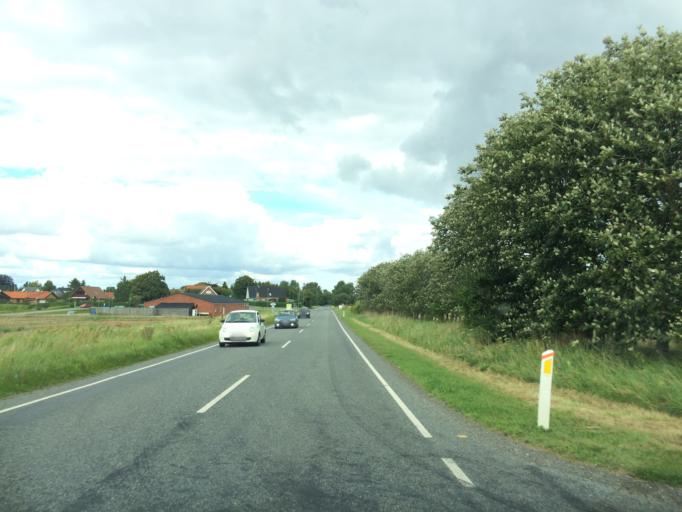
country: DK
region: South Denmark
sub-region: Assens Kommune
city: Tommerup
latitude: 55.2475
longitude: 10.2276
